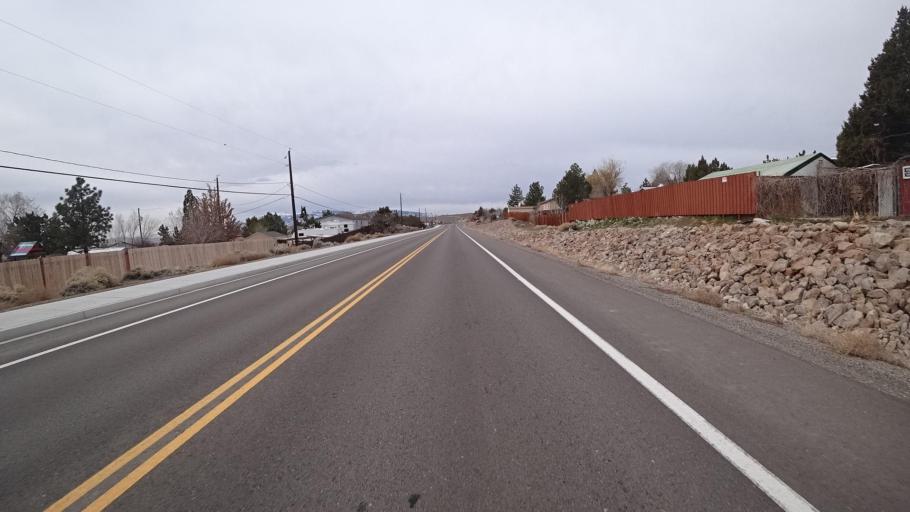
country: US
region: Nevada
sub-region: Washoe County
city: Sun Valley
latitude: 39.6109
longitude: -119.7764
